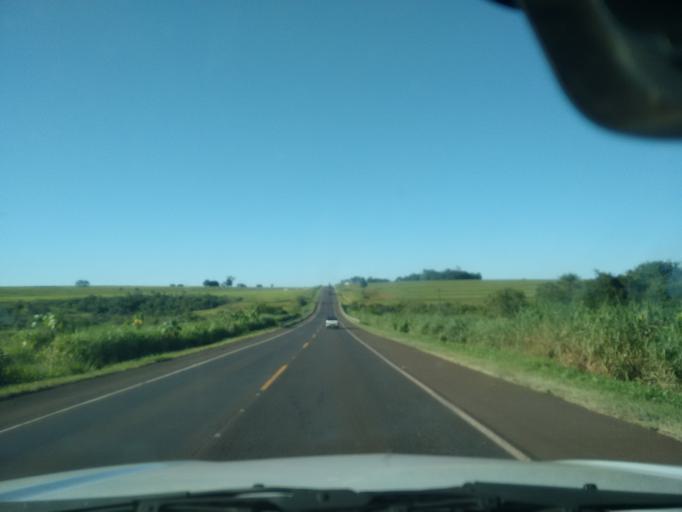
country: PY
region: Canindeyu
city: Salto del Guaira
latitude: -23.9824
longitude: -54.3311
